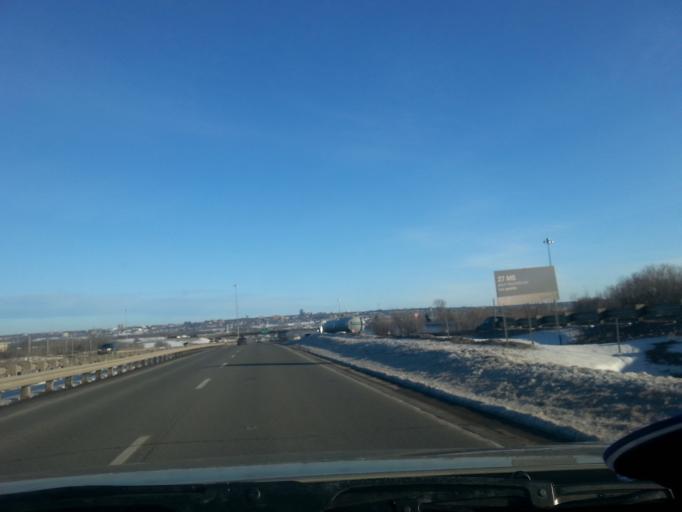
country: CA
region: Quebec
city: L'Ancienne-Lorette
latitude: 46.8126
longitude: -71.3407
